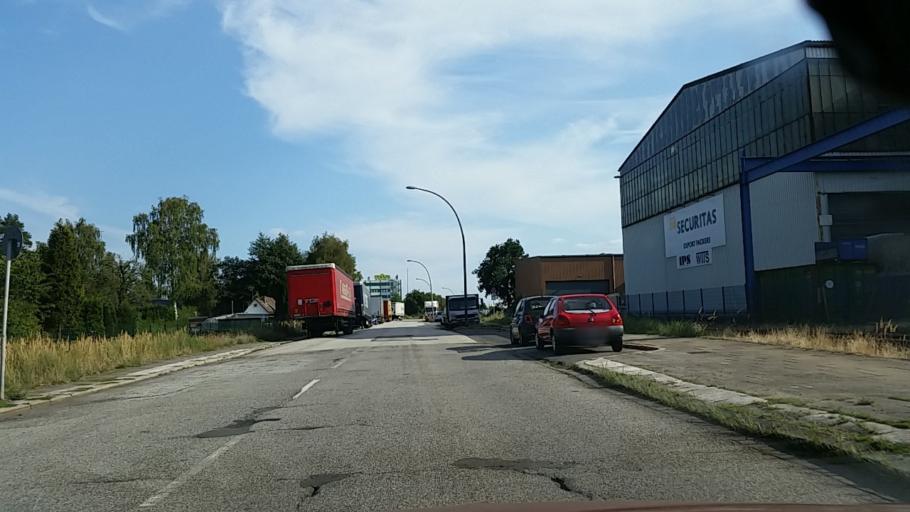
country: DE
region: Hamburg
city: Marienthal
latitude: 53.5194
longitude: 10.0860
